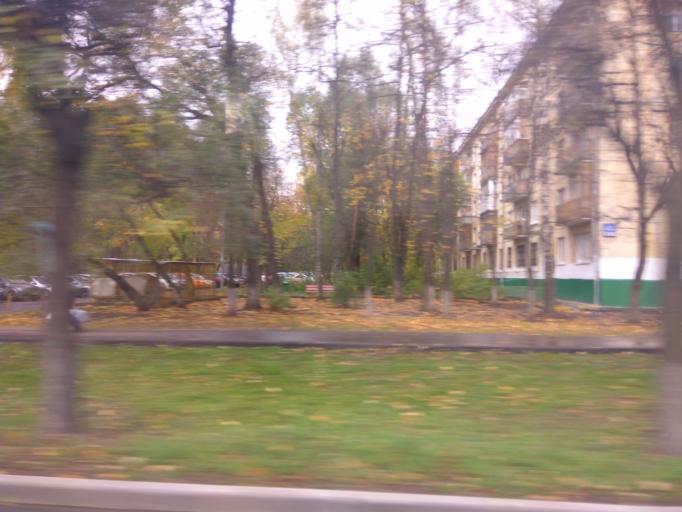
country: RU
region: Moscow
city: Tsaritsyno
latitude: 55.6280
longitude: 37.6521
